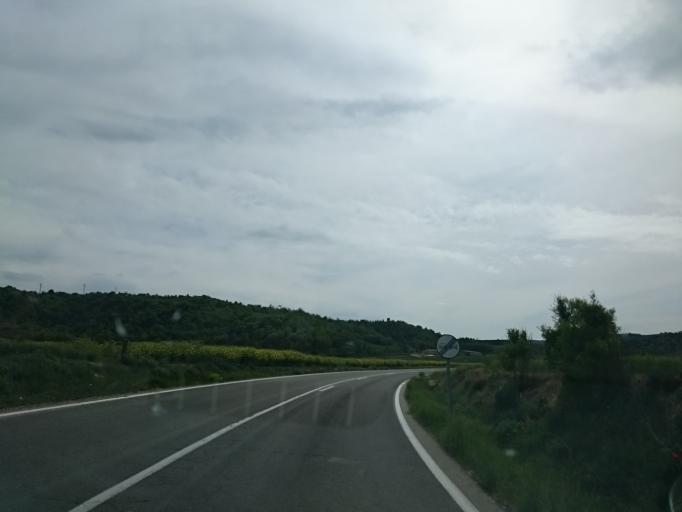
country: ES
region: Catalonia
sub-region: Provincia de Lleida
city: Tora de Riubregos
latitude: 41.7950
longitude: 1.4014
